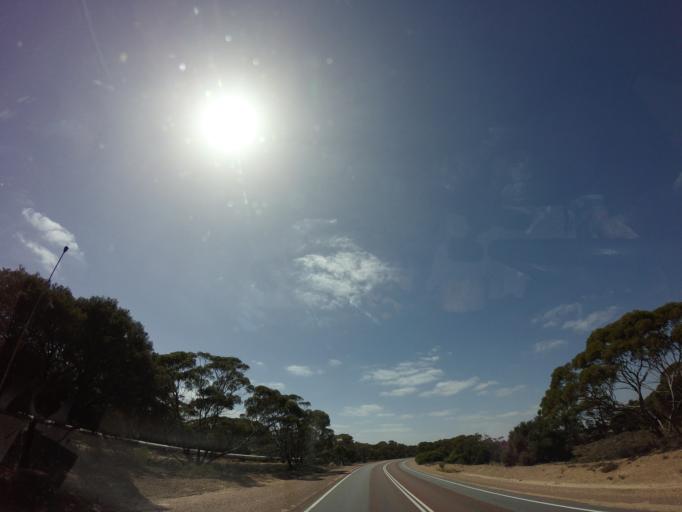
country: AU
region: South Australia
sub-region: Kimba
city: Caralue
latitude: -33.0909
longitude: 135.5122
